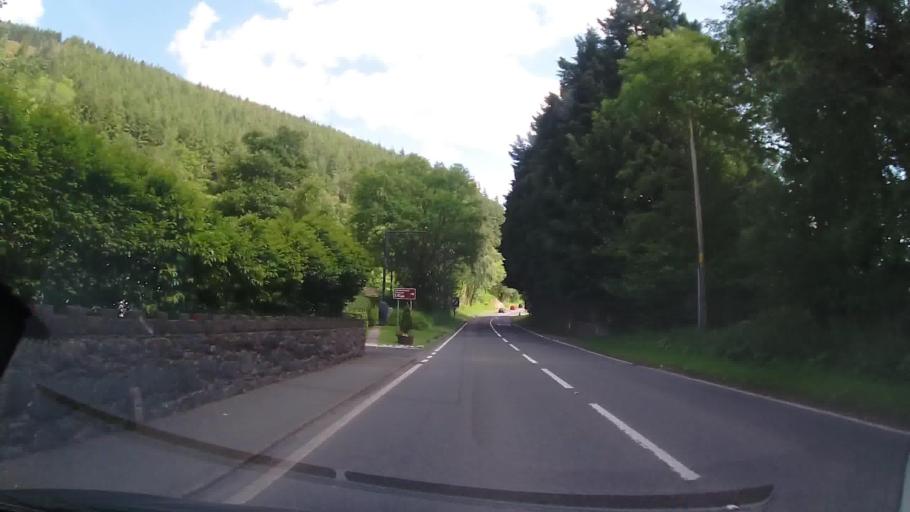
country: GB
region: Wales
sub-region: Gwynedd
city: Corris
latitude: 52.7103
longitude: -3.6889
